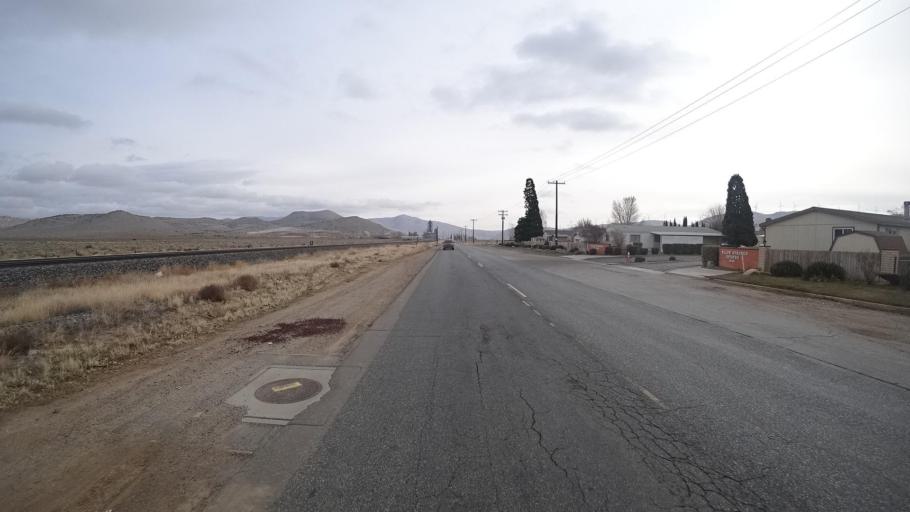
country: US
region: California
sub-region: Kern County
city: Tehachapi
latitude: 35.1242
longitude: -118.3892
